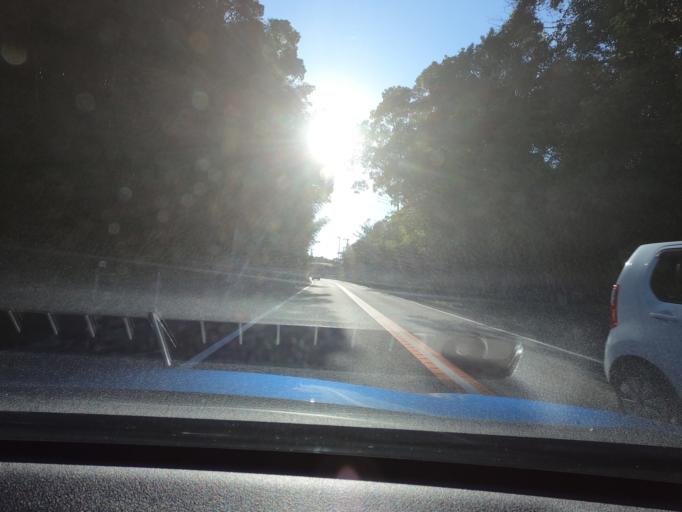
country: JP
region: Kumamoto
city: Minamata
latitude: 32.1670
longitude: 130.3768
